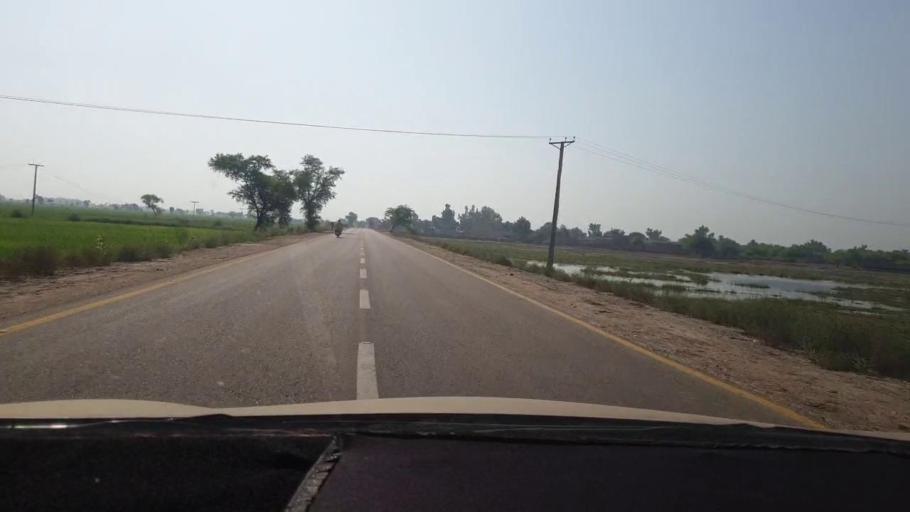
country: PK
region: Sindh
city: Miro Khan
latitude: 27.7252
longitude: 68.1374
